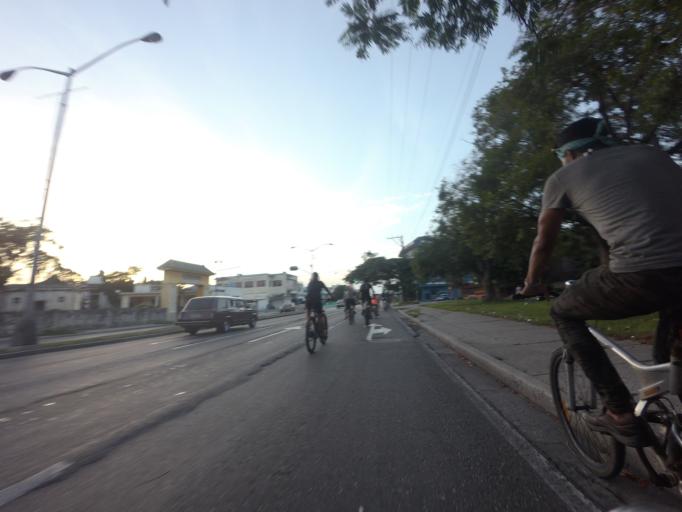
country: CU
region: La Habana
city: Havana
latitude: 23.1194
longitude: -82.4029
